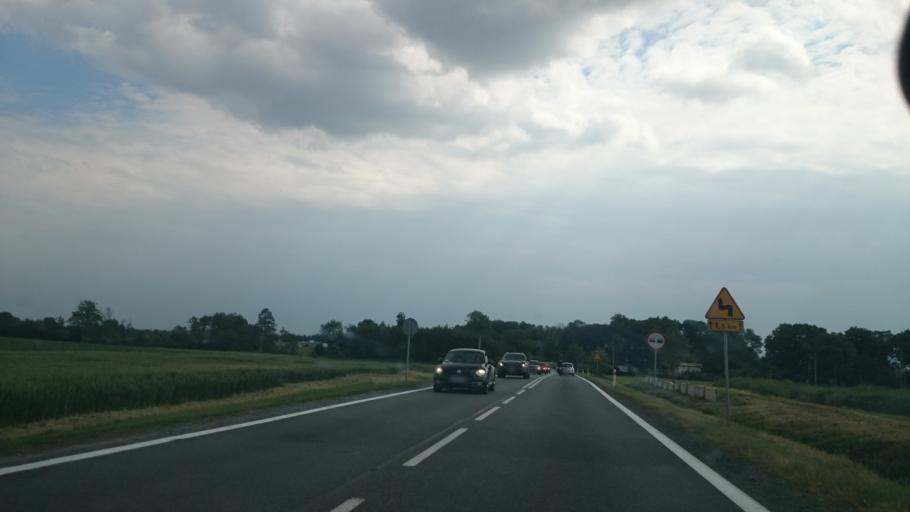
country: PL
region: Lower Silesian Voivodeship
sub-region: Powiat wroclawski
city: Jordanow Slaski
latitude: 50.8797
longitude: 16.8596
